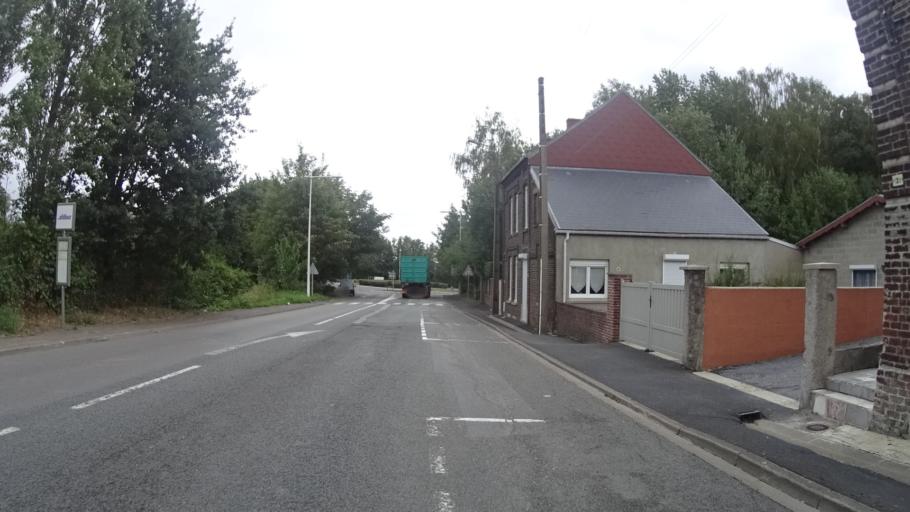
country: FR
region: Nord-Pas-de-Calais
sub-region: Departement du Nord
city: Hautmont
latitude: 50.2446
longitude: 3.9026
